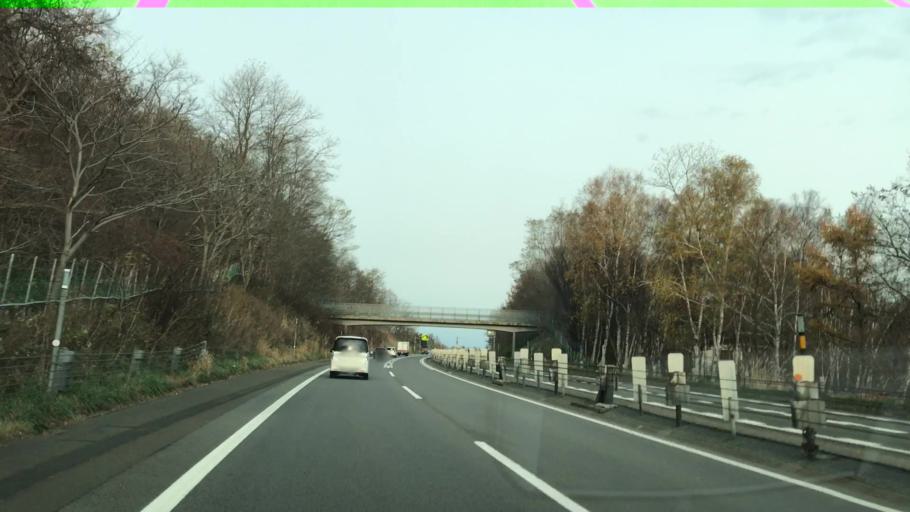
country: JP
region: Hokkaido
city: Otaru
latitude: 43.1478
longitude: 141.1315
